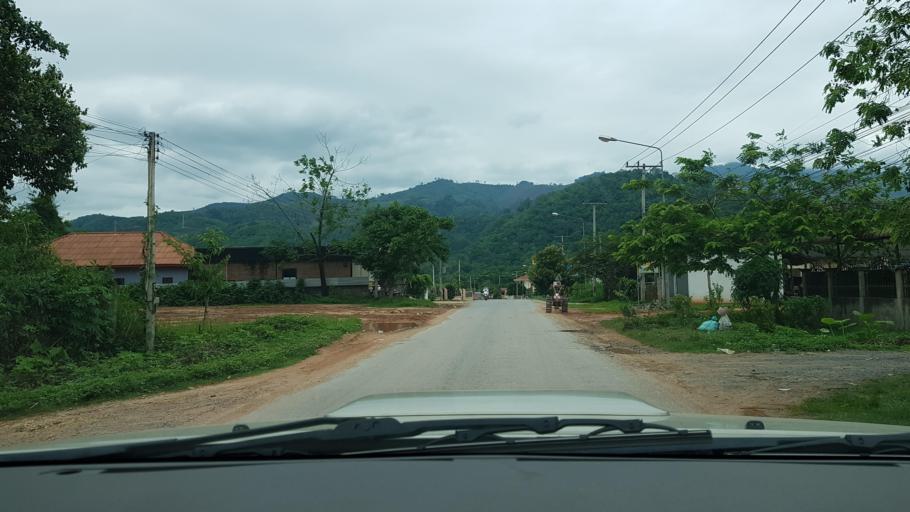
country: LA
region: Oudomxai
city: Muang Xay
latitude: 20.6980
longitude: 102.0000
